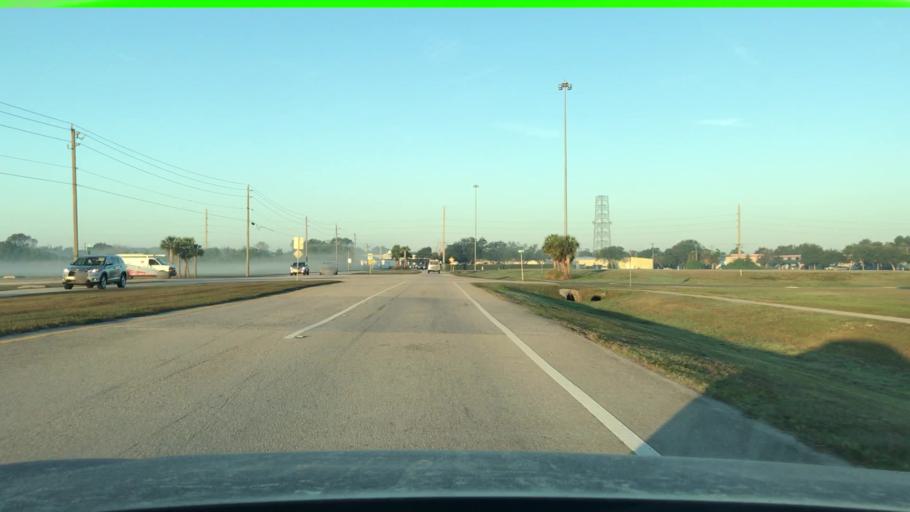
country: US
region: Florida
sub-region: Sarasota County
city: Fruitville
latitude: 27.3258
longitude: -82.4427
